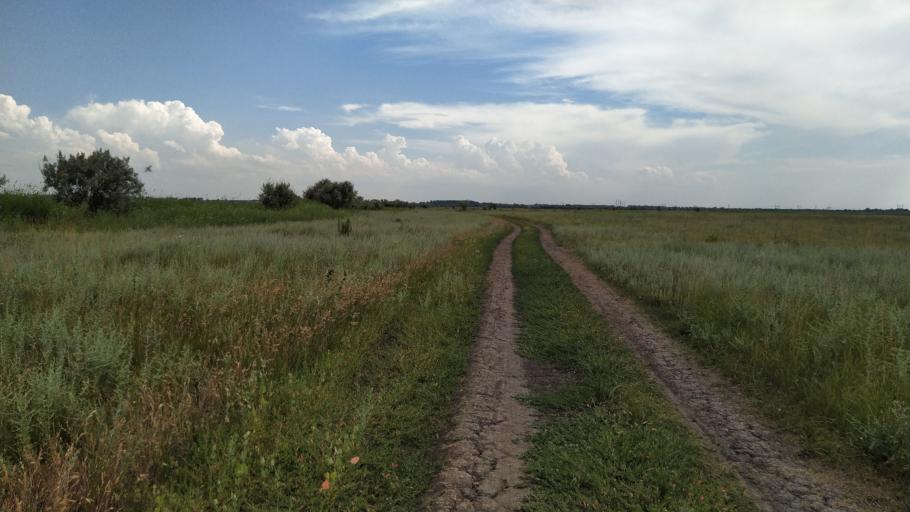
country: RU
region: Rostov
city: Kuleshovka
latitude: 47.1340
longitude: 39.6309
